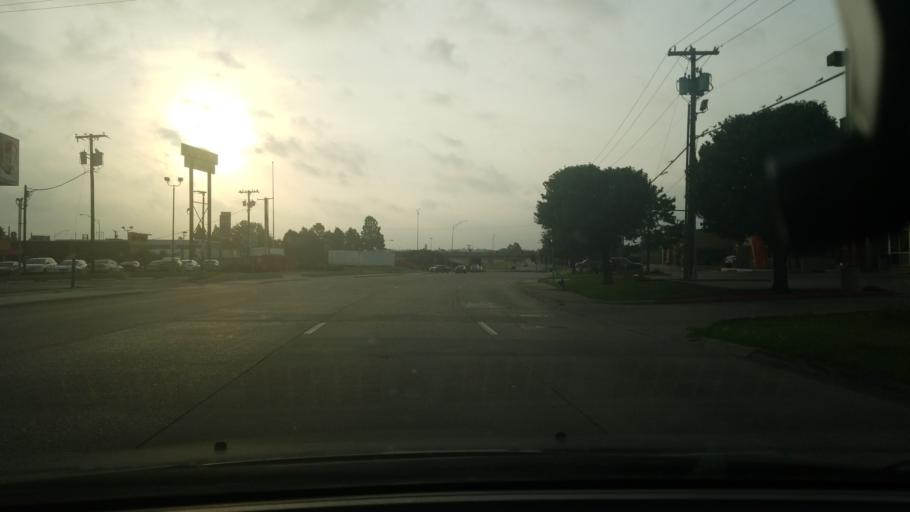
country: US
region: Texas
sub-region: Dallas County
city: Mesquite
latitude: 32.7678
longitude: -96.6250
